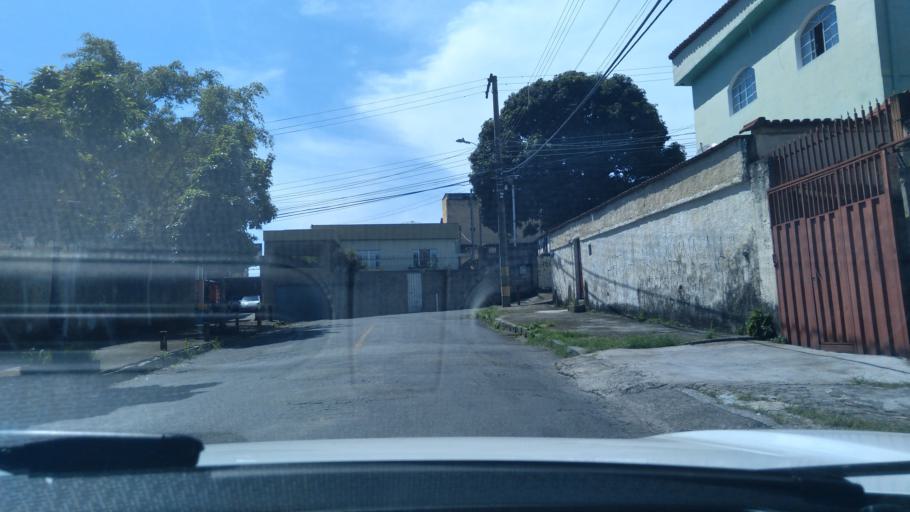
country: BR
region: Minas Gerais
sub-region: Contagem
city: Contagem
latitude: -19.9221
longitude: -44.0045
